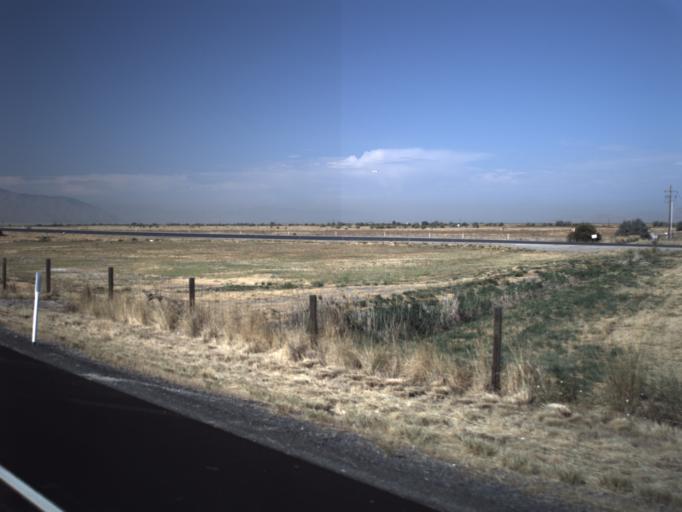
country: US
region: Utah
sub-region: Davis County
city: West Bountiful
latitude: 40.8859
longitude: -111.9376
